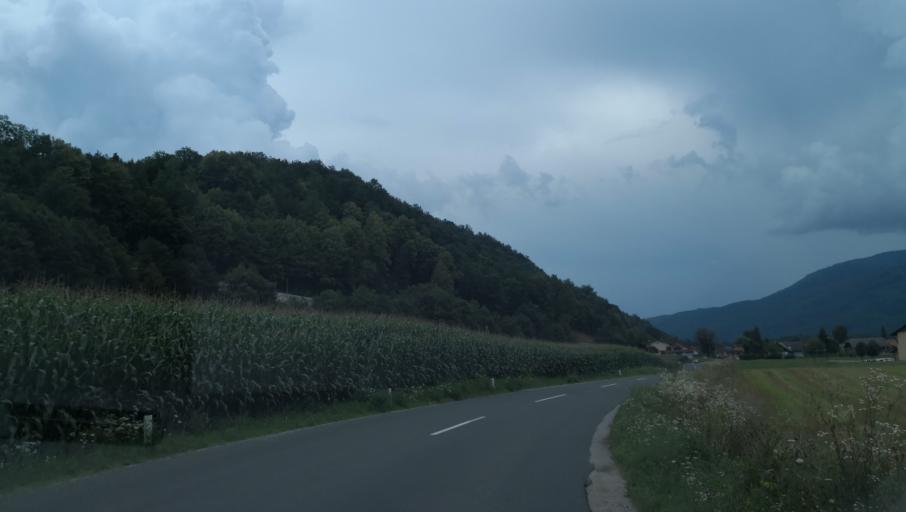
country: SI
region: Zuzemberk
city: Zuzemberk
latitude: 45.8143
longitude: 14.9632
